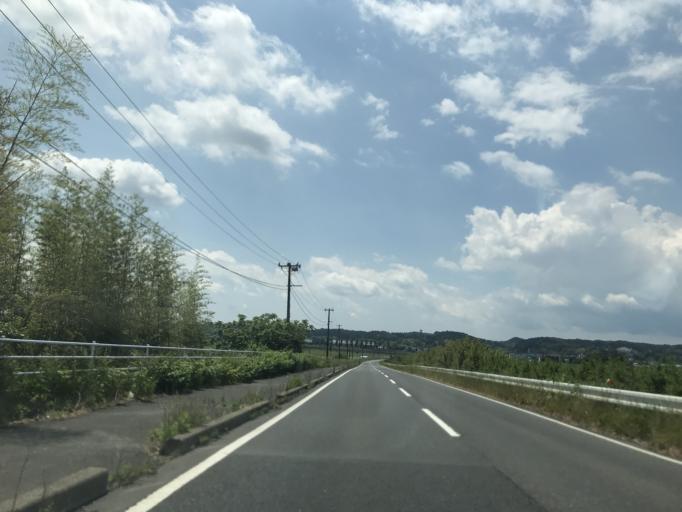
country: JP
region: Miyagi
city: Kogota
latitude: 38.5261
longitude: 141.0579
